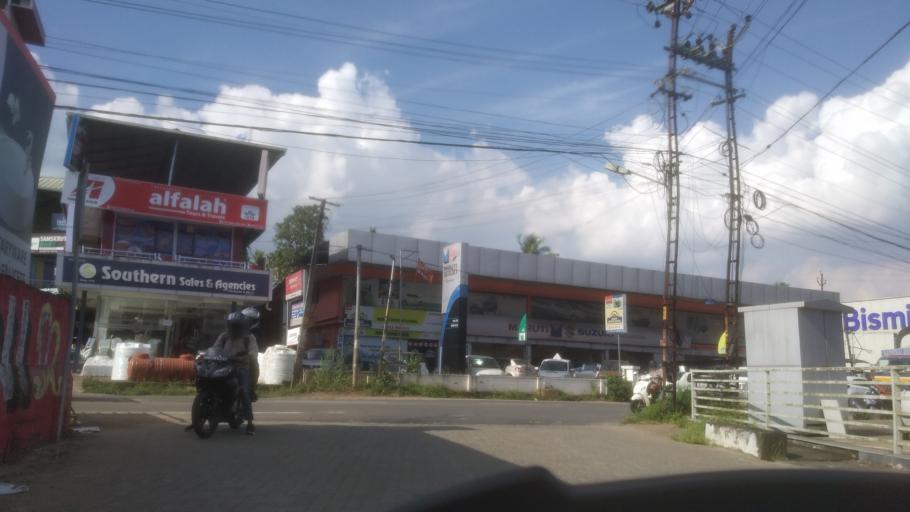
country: IN
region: Kerala
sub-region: Ernakulam
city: Muvattupula
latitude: 9.9926
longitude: 76.5870
